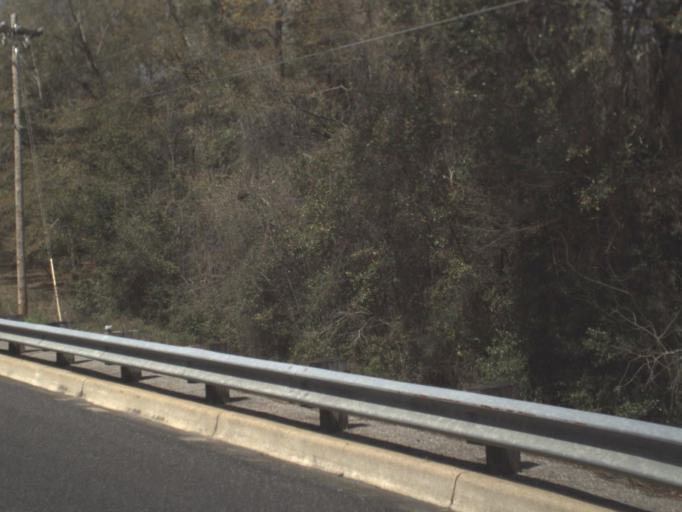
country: US
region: Florida
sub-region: Gadsden County
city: Quincy
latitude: 30.5672
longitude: -84.5449
